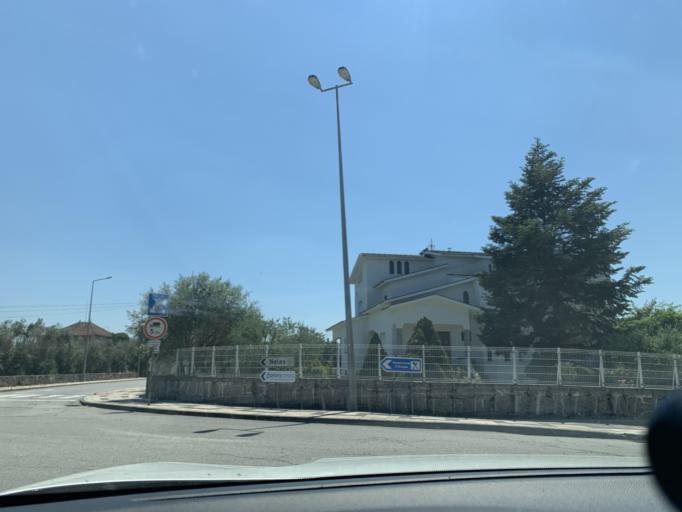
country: PT
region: Viseu
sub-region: Nelas
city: Nelas
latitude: 40.5397
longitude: -7.8459
